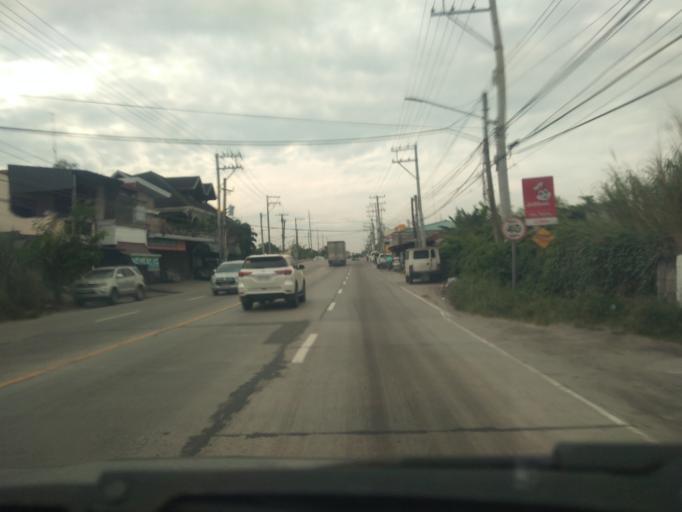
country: PH
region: Central Luzon
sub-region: Province of Pampanga
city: San Fernando
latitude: 15.0292
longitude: 120.6969
